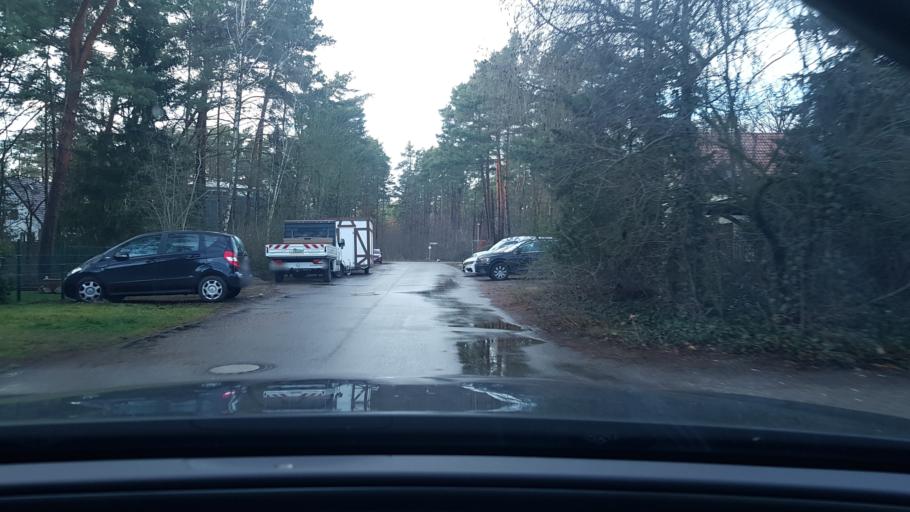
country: DE
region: Berlin
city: Muggelheim
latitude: 52.4226
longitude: 13.6734
